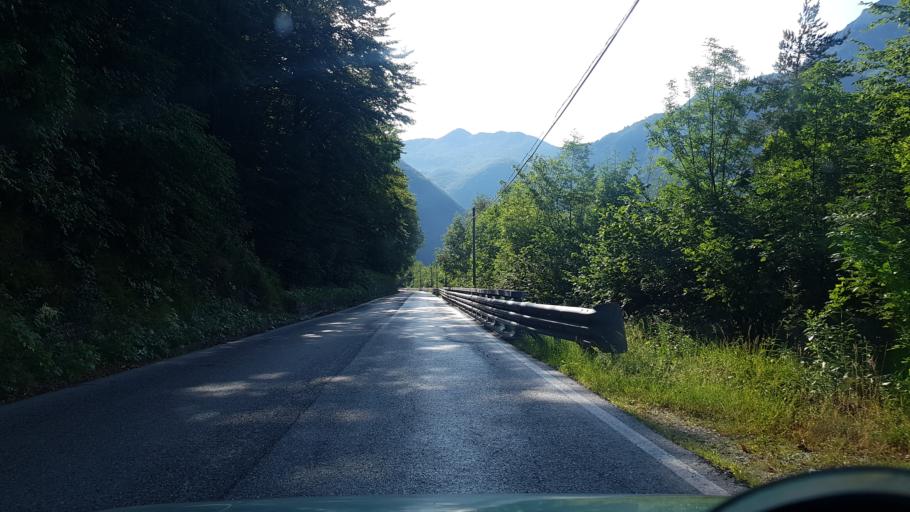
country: IT
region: Friuli Venezia Giulia
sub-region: Provincia di Udine
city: Lusevera
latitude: 46.3069
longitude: 13.2840
